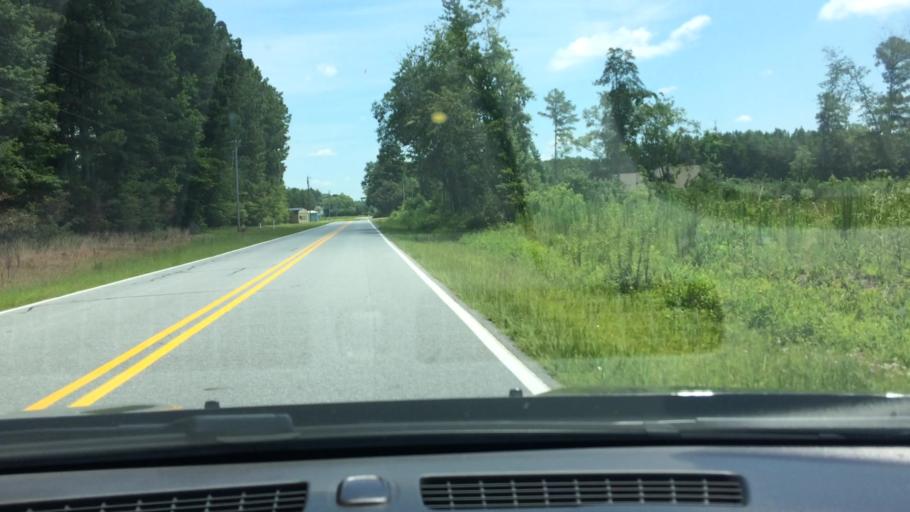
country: US
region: North Carolina
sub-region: Pitt County
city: Windsor
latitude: 35.4966
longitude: -77.3449
